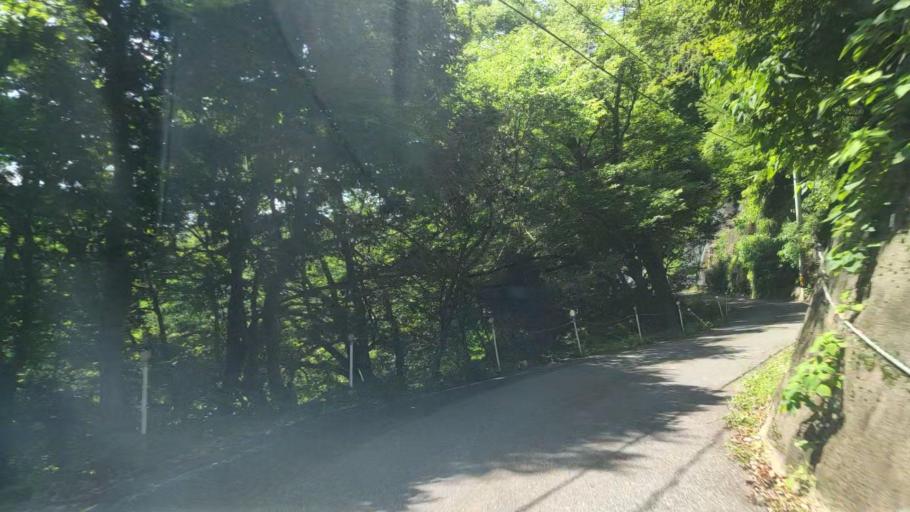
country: JP
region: Gifu
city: Godo
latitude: 35.6904
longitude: 136.5841
